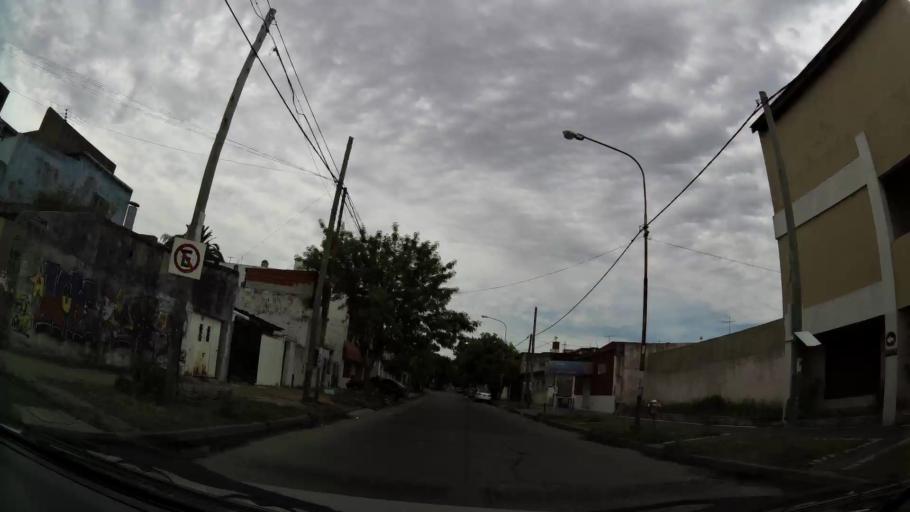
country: AR
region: Buenos Aires
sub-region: Partido de Lanus
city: Lanus
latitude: -34.6852
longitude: -58.3899
